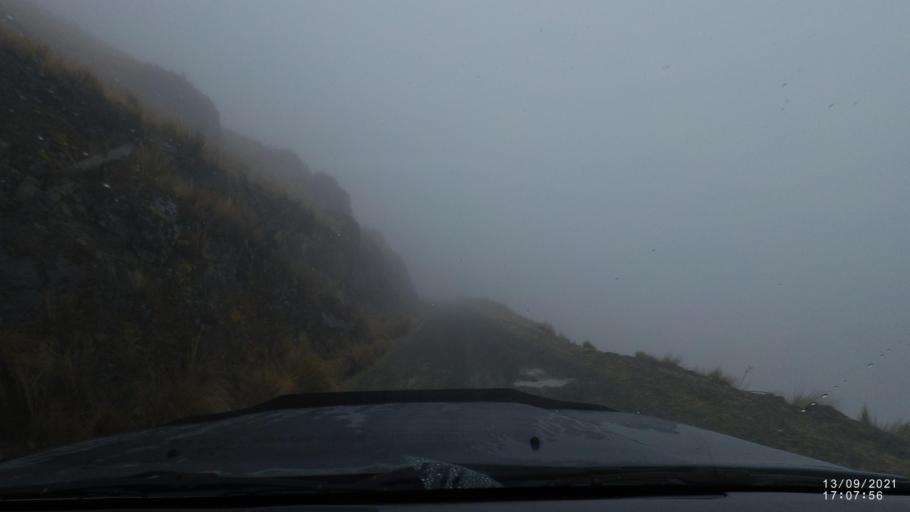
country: BO
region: Cochabamba
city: Colomi
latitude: -17.3290
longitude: -65.7283
